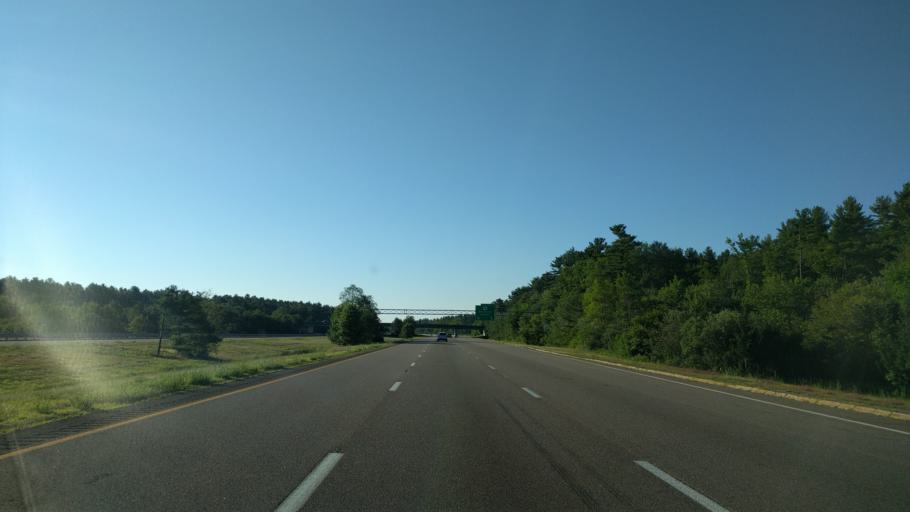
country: US
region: Massachusetts
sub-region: Bristol County
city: Mansfield Center
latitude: 42.0091
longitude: -71.2284
